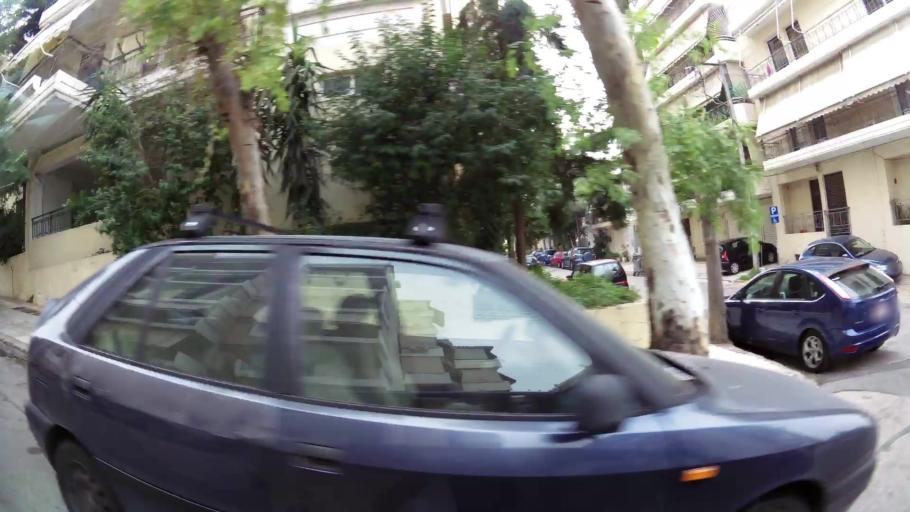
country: GR
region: Attica
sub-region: Nomarchia Athinas
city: Nea Ionia
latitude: 38.0368
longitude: 23.7570
